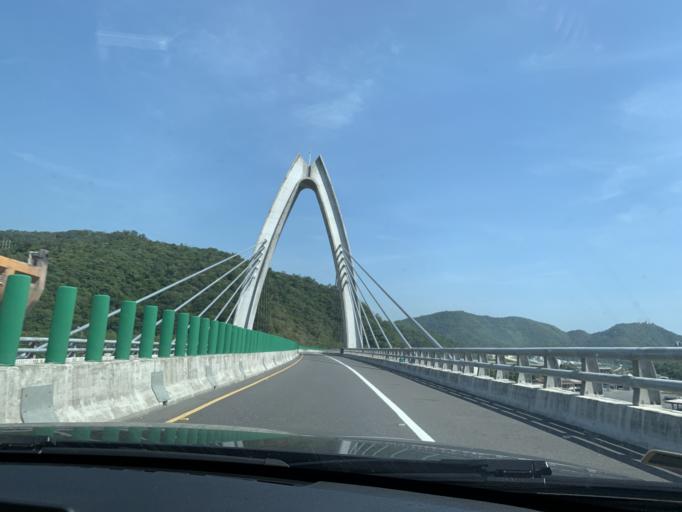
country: TW
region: Taiwan
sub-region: Yilan
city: Yilan
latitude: 24.5736
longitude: 121.8474
